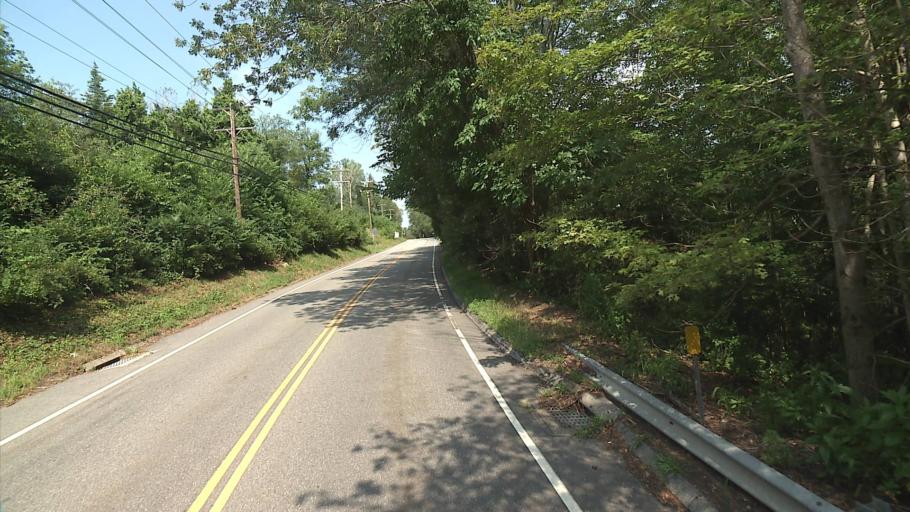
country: US
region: Connecticut
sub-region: New London County
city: Montville Center
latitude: 41.5757
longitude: -72.1924
